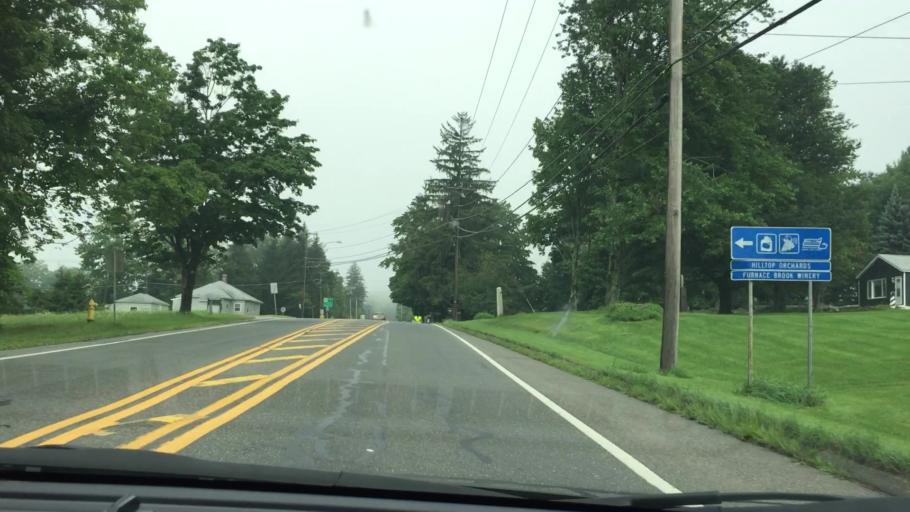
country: US
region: Massachusetts
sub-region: Berkshire County
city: Richmond
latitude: 42.4315
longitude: -73.3308
